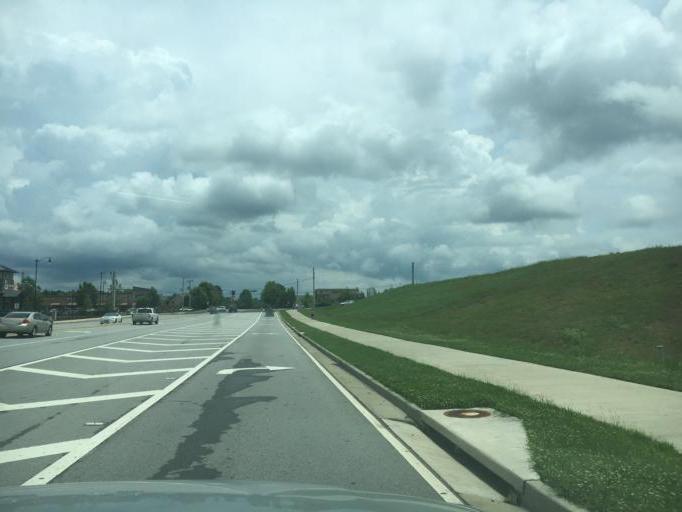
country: US
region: Georgia
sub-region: Jackson County
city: Braselton
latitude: 34.1214
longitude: -83.8294
